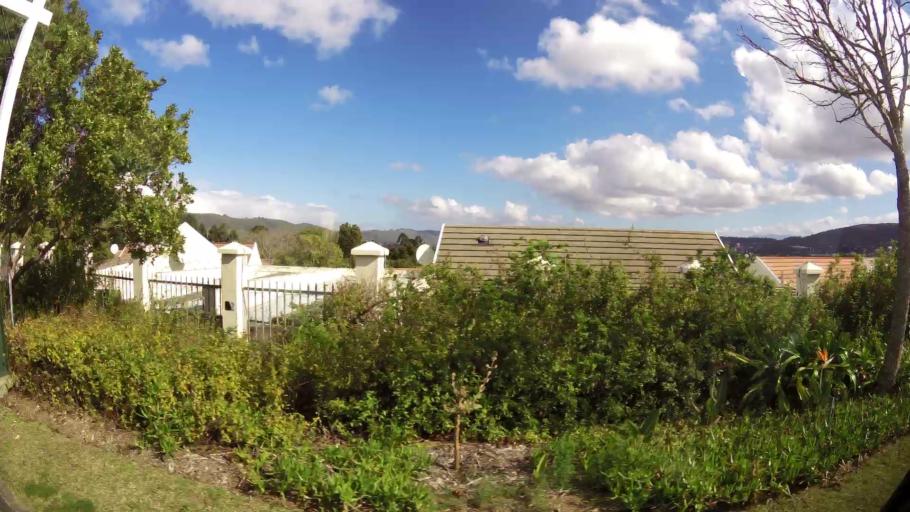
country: ZA
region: Western Cape
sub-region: Eden District Municipality
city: Knysna
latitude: -34.0529
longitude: 23.0768
